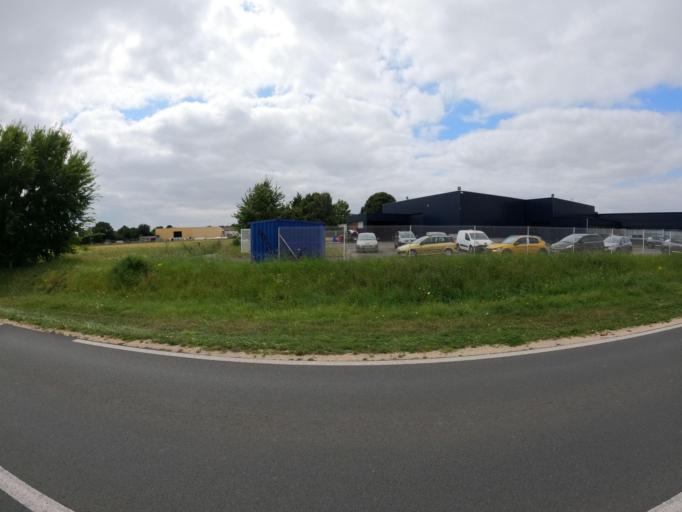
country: FR
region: Poitou-Charentes
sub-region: Departement de la Vienne
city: Civray
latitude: 46.1619
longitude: 0.3003
